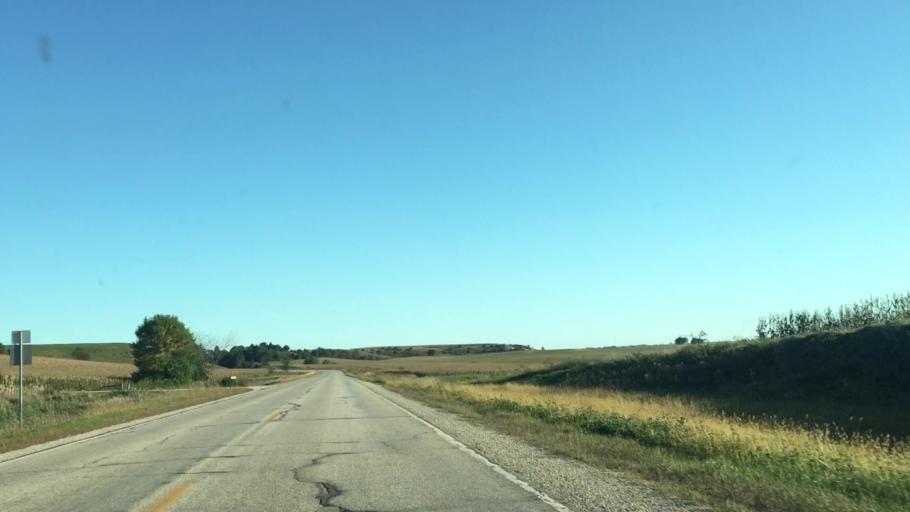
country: US
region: Minnesota
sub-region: Fillmore County
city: Chatfield
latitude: 43.8513
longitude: -92.1079
